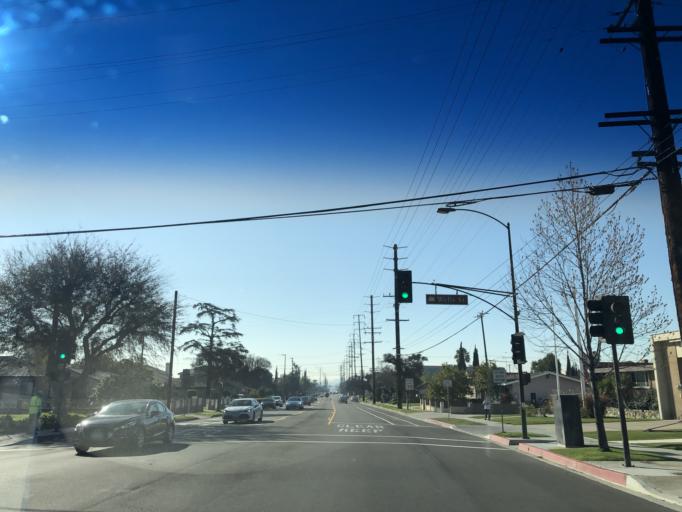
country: US
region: California
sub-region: Los Angeles County
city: East San Gabriel
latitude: 34.0846
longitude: -118.0996
